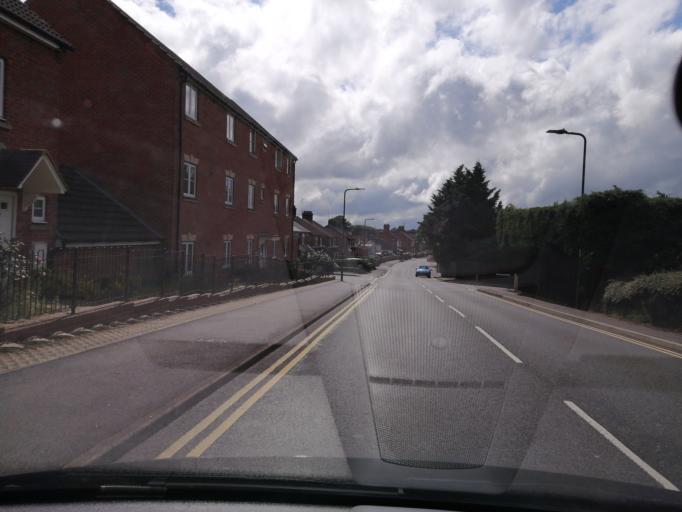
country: GB
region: England
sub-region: Peterborough
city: Peterborough
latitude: 52.5578
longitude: -0.2445
